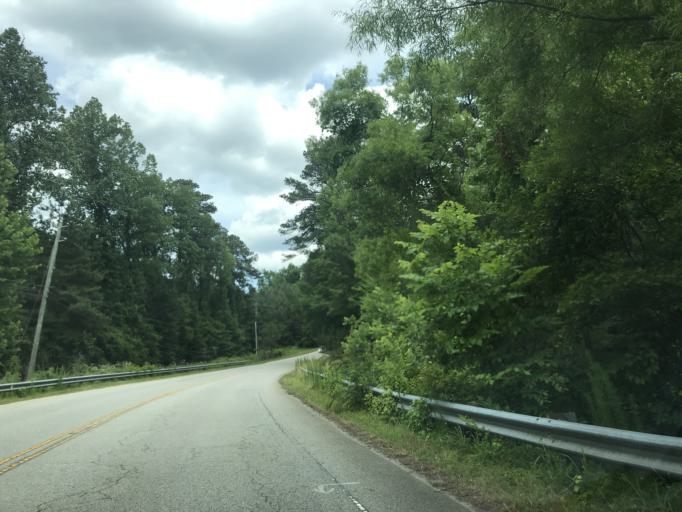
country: US
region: North Carolina
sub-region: Wake County
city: West Raleigh
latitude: 35.9134
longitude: -78.6792
